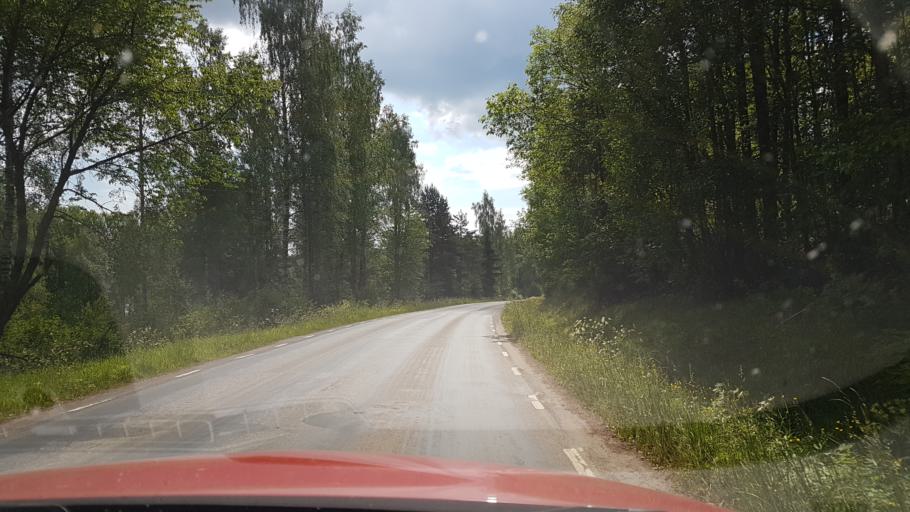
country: SE
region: Vaestra Goetaland
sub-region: Hjo Kommun
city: Hjo
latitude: 58.3100
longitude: 14.1891
